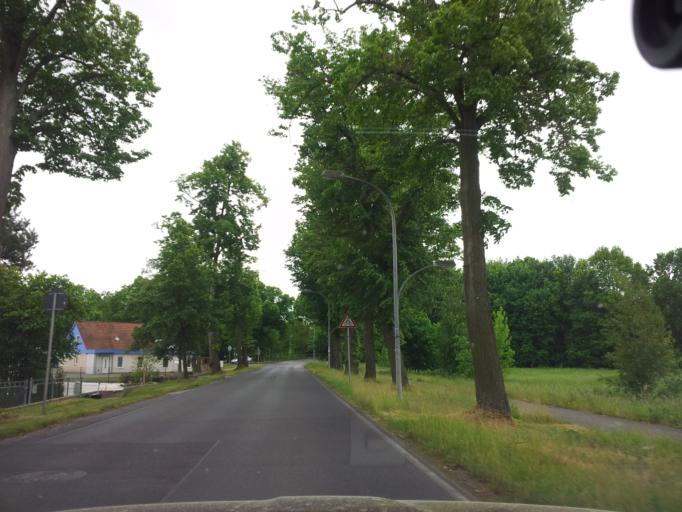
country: DE
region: Brandenburg
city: Dallgow-Doeberitz
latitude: 52.5464
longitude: 13.0627
